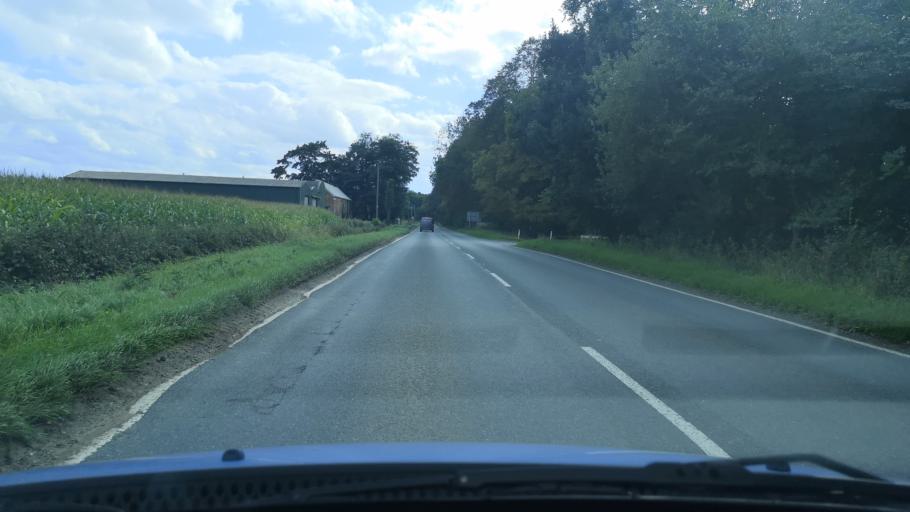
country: GB
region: England
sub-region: North Lincolnshire
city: Crowle
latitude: 53.5830
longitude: -0.8201
